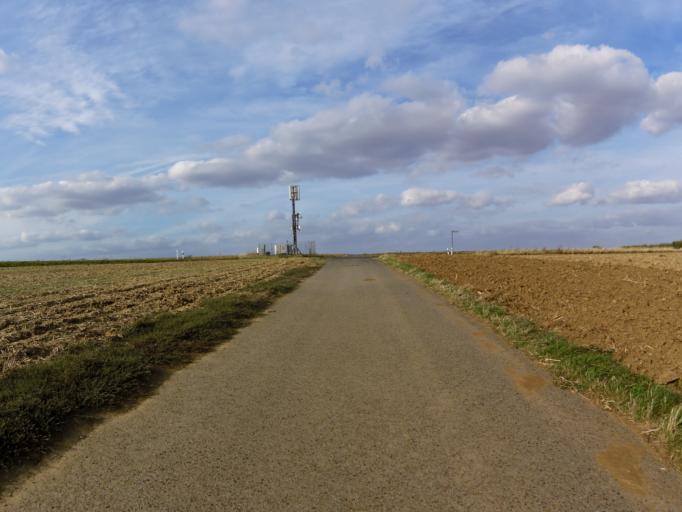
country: DE
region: Bavaria
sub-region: Regierungsbezirk Unterfranken
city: Reichenberg
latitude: 49.7156
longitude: 9.9478
